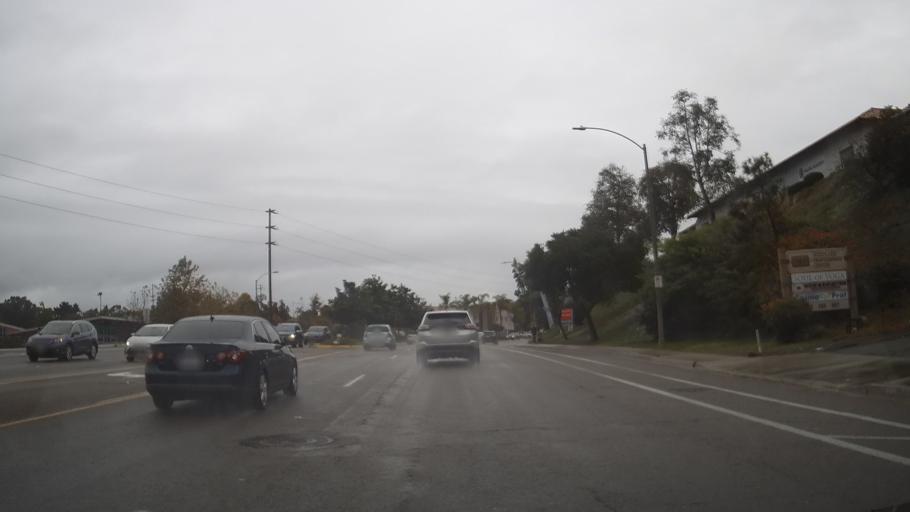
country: US
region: California
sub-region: San Diego County
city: Encinitas
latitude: 33.0477
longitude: -117.2787
